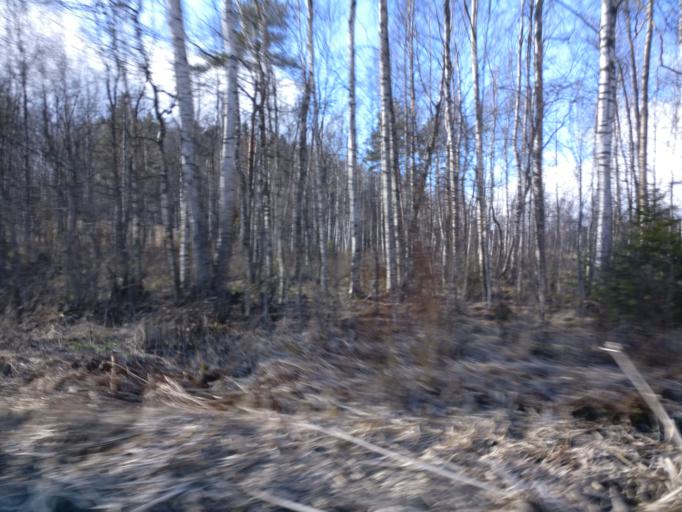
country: FI
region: Uusimaa
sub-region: Helsinki
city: Karjalohja
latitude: 60.2735
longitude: 23.6618
